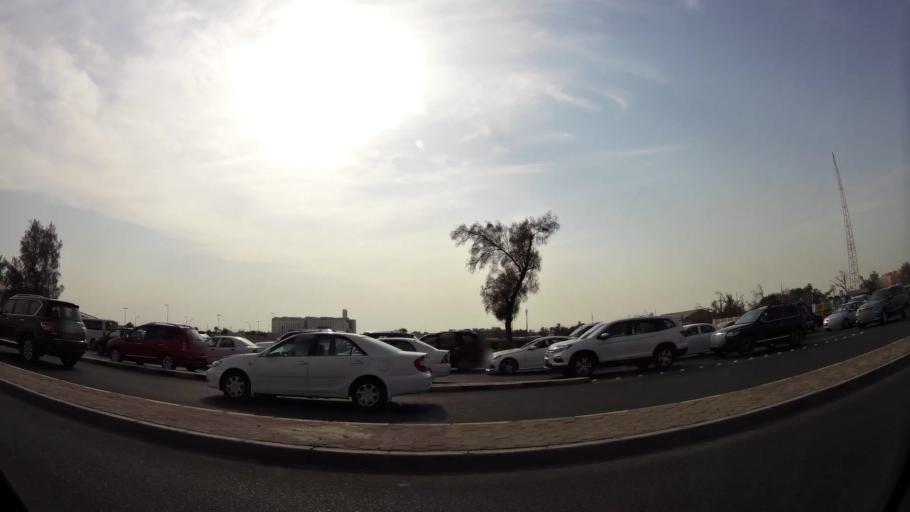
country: KW
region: Al Asimah
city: Ash Shamiyah
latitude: 29.3221
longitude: 47.9590
